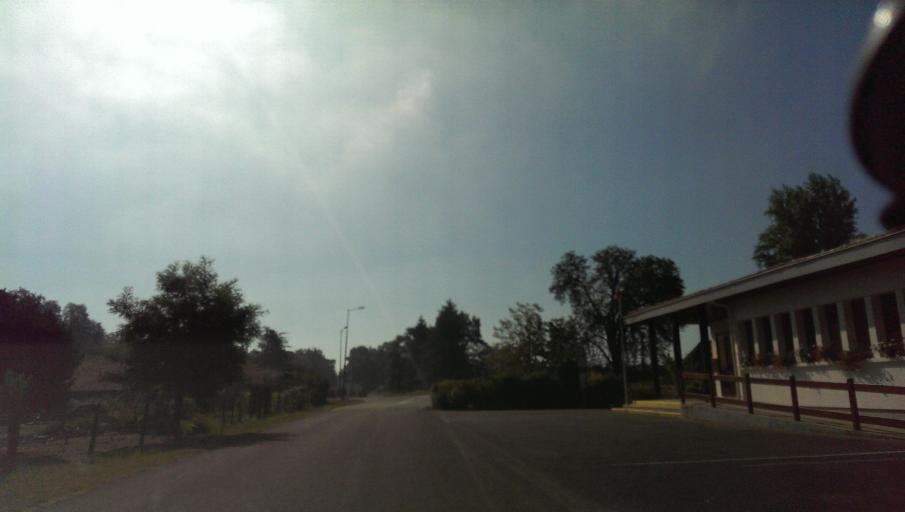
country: FR
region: Aquitaine
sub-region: Departement des Landes
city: Gabarret
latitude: 44.1033
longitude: -0.0155
